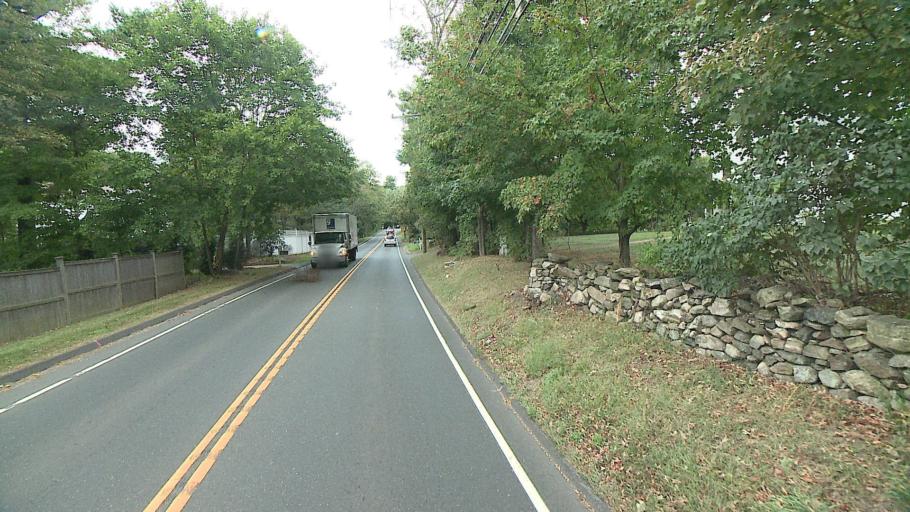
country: US
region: Connecticut
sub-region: Fairfield County
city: Westport
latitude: 41.1672
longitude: -73.3841
